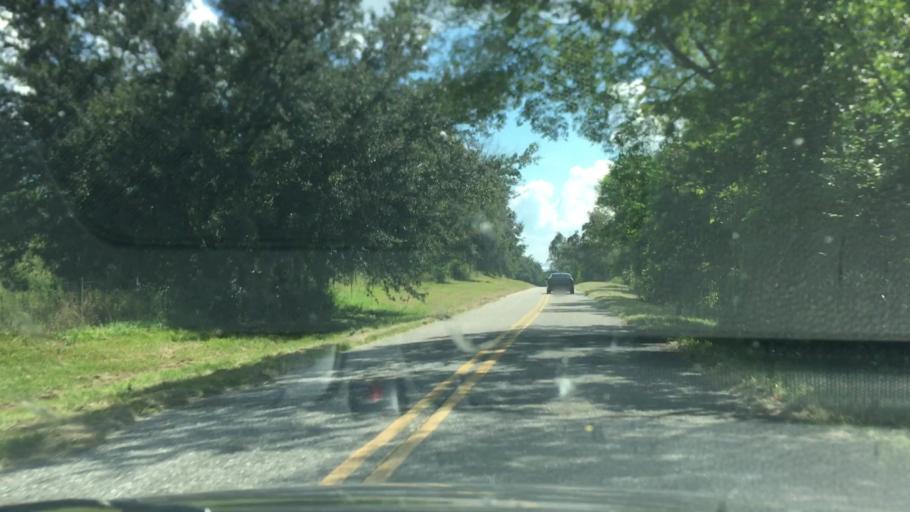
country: US
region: Florida
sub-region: Lake County
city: Montverde
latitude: 28.6375
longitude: -81.7203
